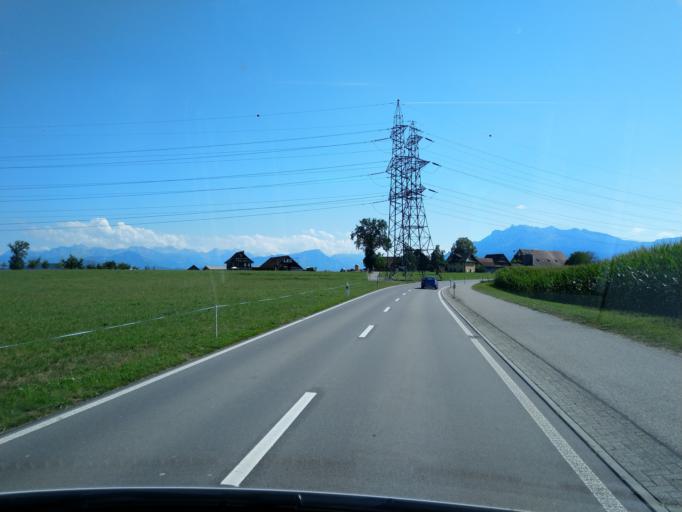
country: CH
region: Lucerne
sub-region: Hochdorf District
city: Emmen
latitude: 47.1112
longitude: 8.2915
